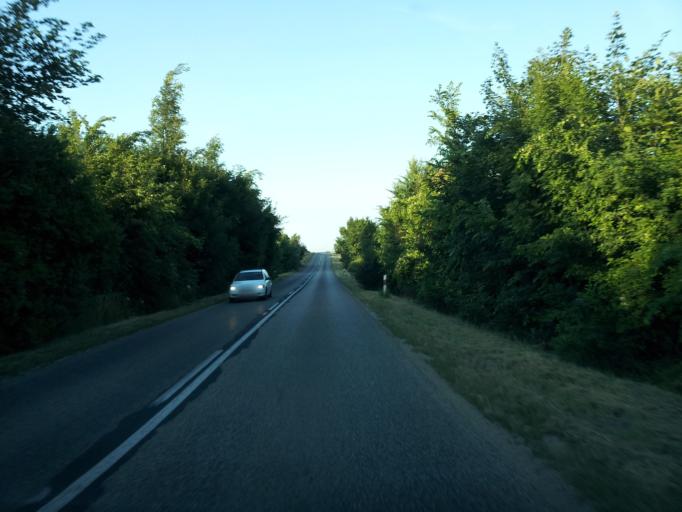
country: HU
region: Veszprem
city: Szentkiralyszabadja
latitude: 47.0623
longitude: 17.9781
